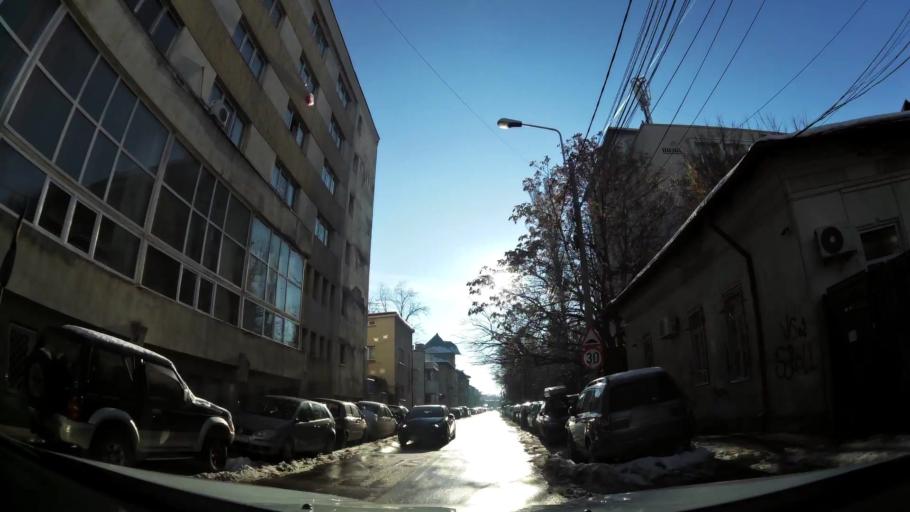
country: RO
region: Bucuresti
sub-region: Municipiul Bucuresti
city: Bucuresti
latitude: 44.4215
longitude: 26.0965
